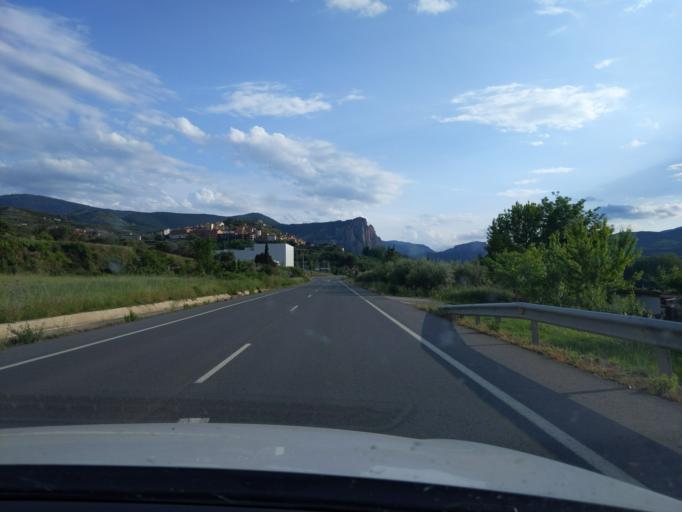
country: ES
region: La Rioja
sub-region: Provincia de La Rioja
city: Nalda
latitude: 42.3431
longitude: -2.4834
